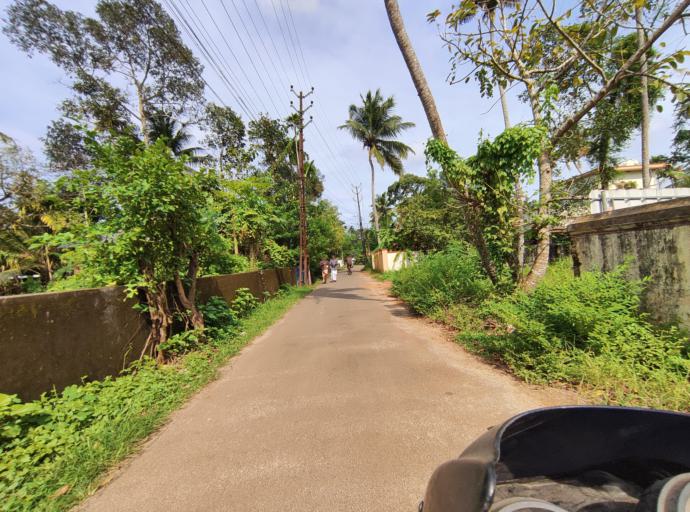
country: IN
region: Kerala
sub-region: Alappuzha
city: Vayalar
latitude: 9.6921
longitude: 76.3407
